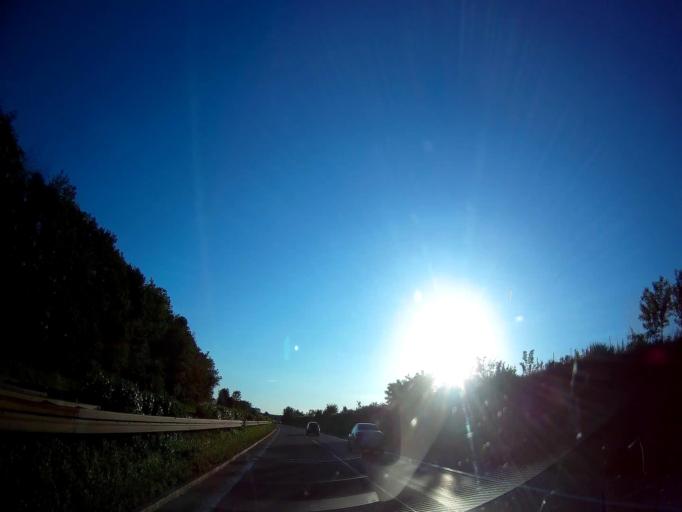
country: DE
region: Bavaria
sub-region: Regierungsbezirk Mittelfranken
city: Altdorf
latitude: 49.3777
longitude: 11.3679
